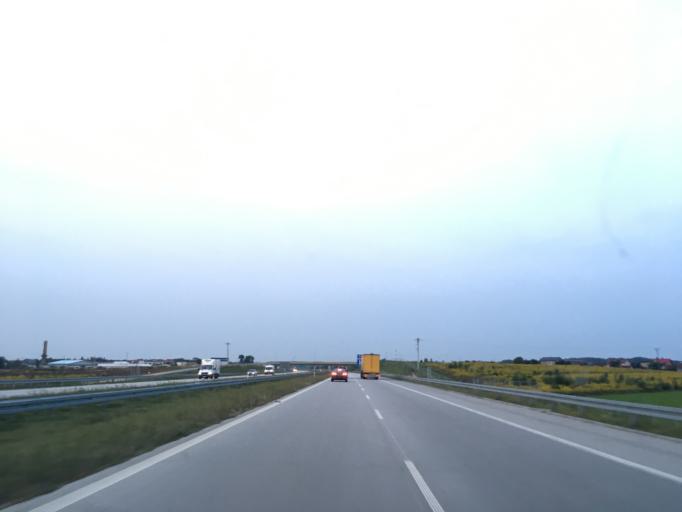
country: PL
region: Lodz Voivodeship
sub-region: Powiat lodzki wschodni
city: Andrespol
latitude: 51.8078
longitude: 19.6299
